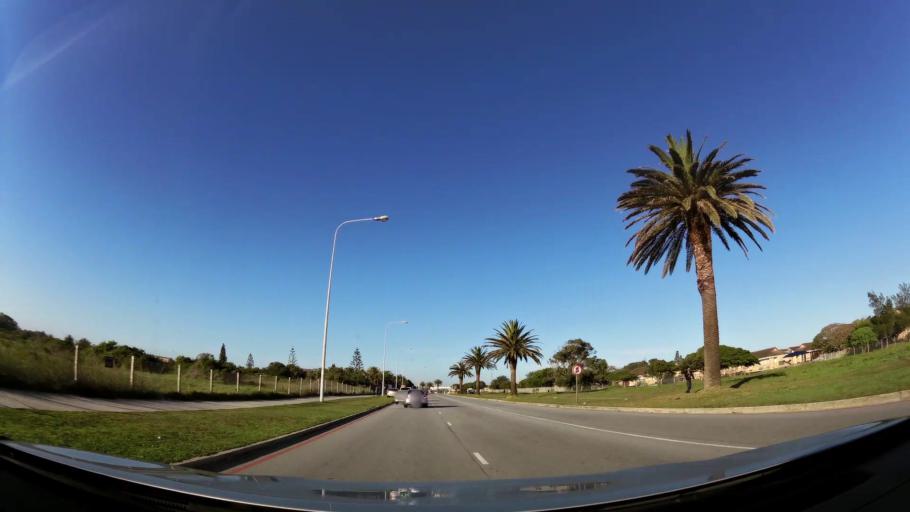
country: ZA
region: Eastern Cape
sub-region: Nelson Mandela Bay Metropolitan Municipality
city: Port Elizabeth
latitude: -33.9967
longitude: 25.6704
